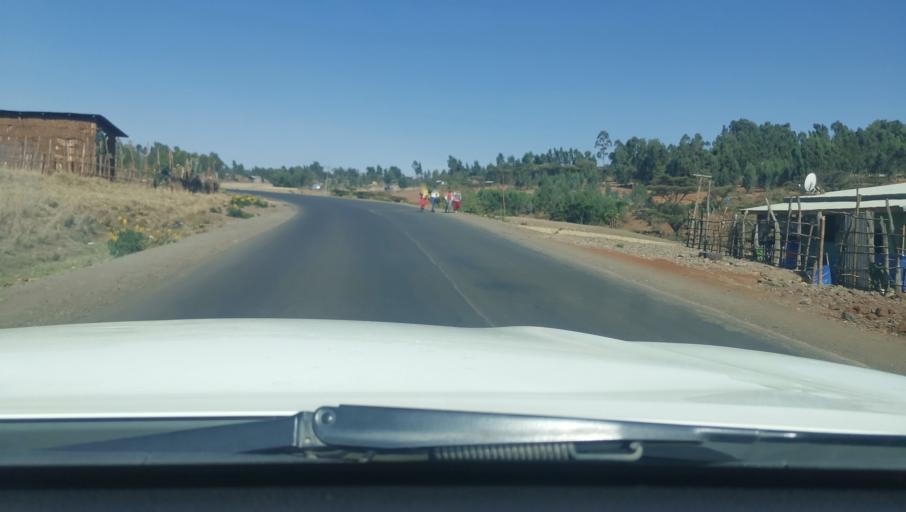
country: ET
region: Oromiya
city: Gedo
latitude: 8.9664
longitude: 37.5281
